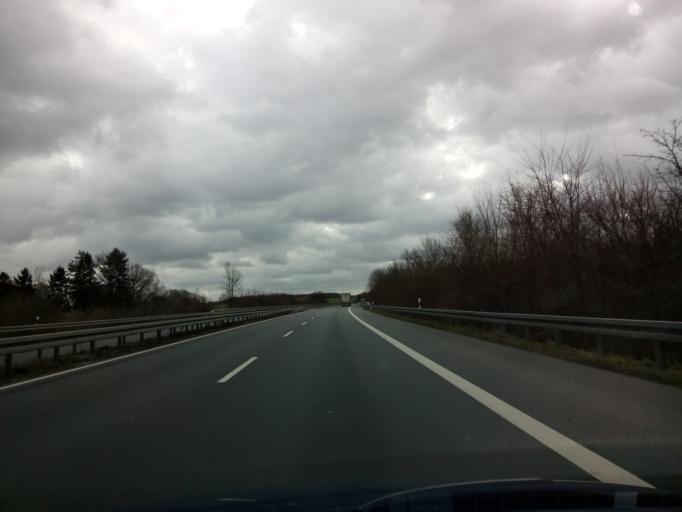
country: DE
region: Lower Saxony
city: Wallenhorst
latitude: 52.3306
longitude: 8.0303
